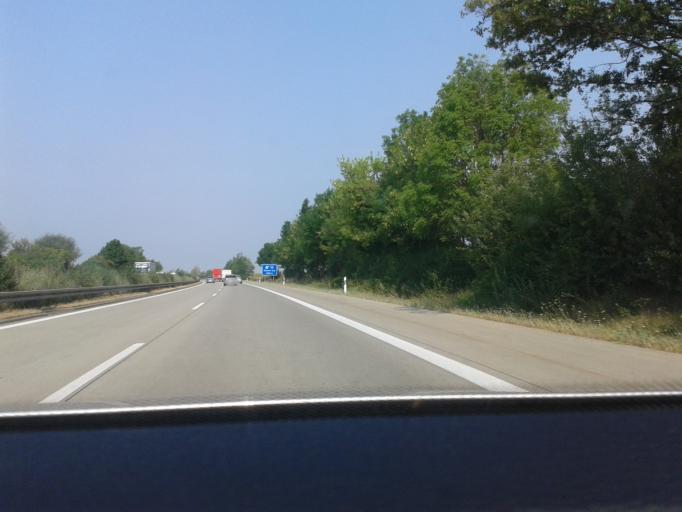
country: DE
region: Saxony
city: Mochau
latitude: 51.1027
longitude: 13.2031
